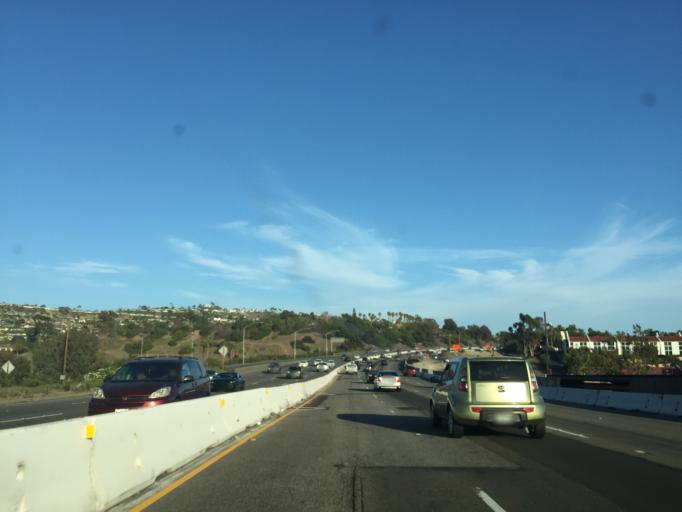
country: US
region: California
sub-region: Orange County
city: San Clemente
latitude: 33.4386
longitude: -117.6217
